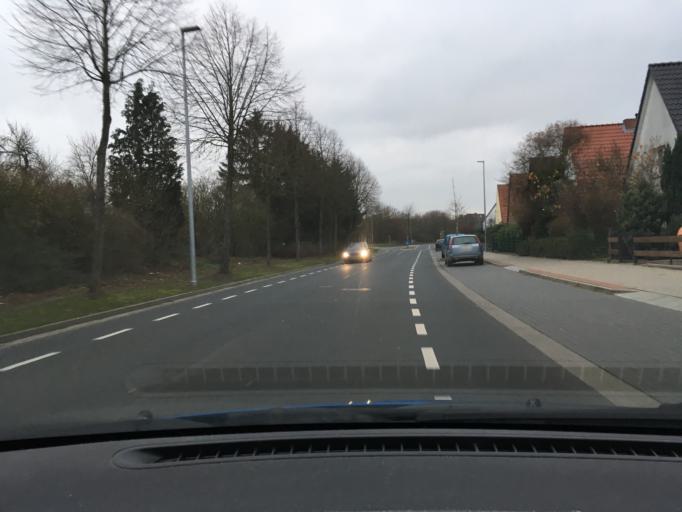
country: DE
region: Lower Saxony
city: Walsrode
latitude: 52.8535
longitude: 9.5830
